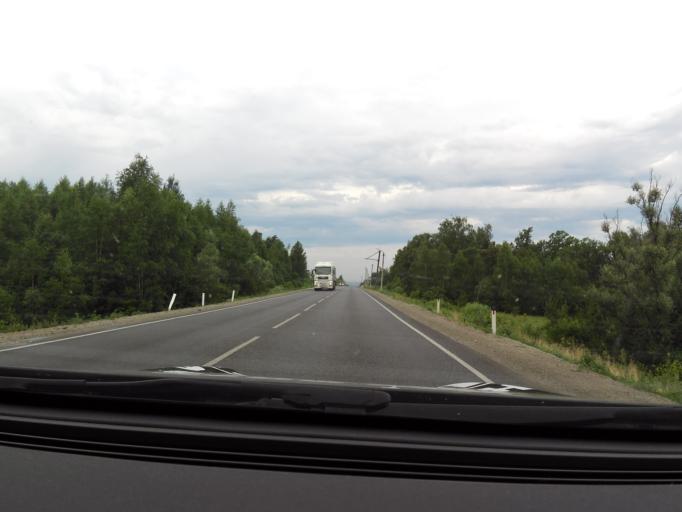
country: RU
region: Bashkortostan
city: Ulu-Telyak
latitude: 54.8424
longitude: 57.0642
